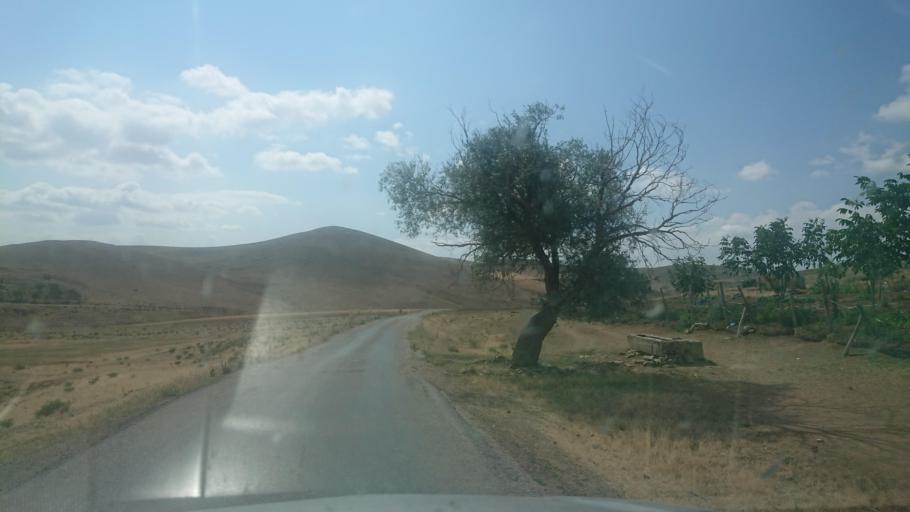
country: TR
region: Aksaray
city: Sariyahsi
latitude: 39.0113
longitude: 33.9466
